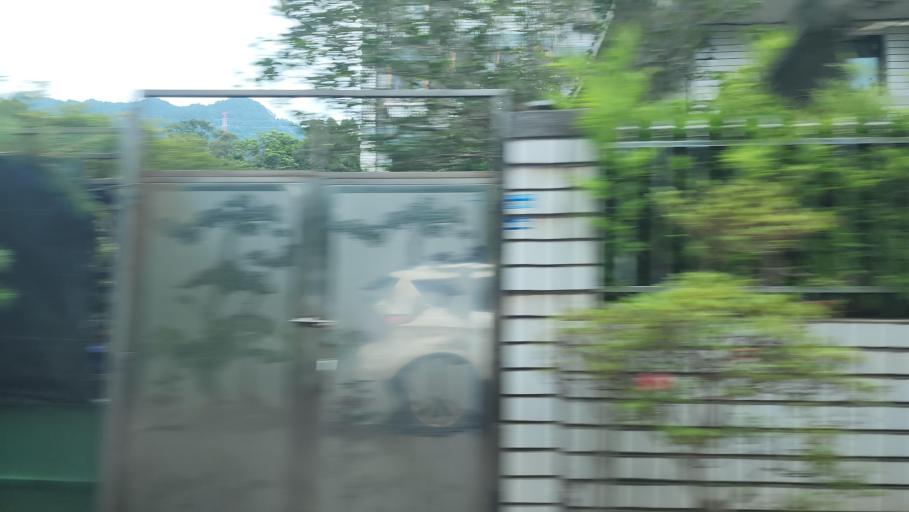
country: TW
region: Taiwan
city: Daxi
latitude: 24.9075
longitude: 121.3920
